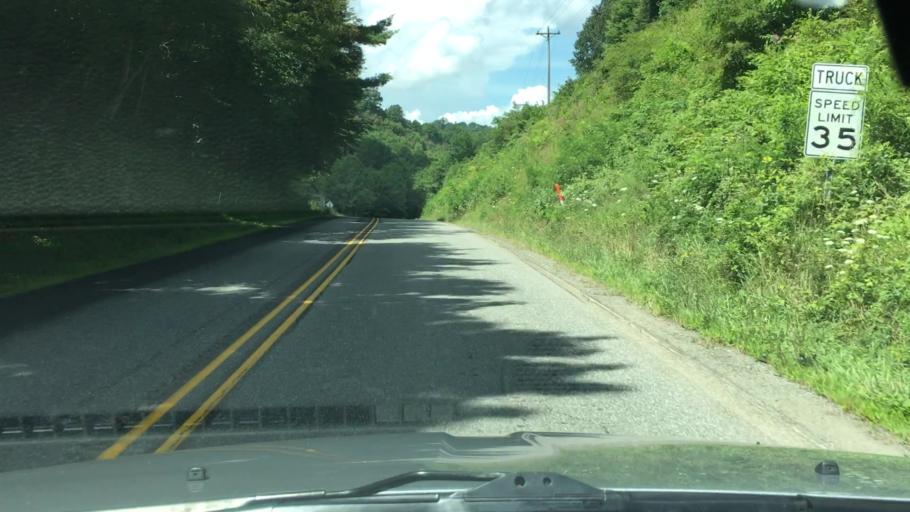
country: US
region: North Carolina
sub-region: Madison County
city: Mars Hill
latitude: 35.9070
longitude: -82.5475
